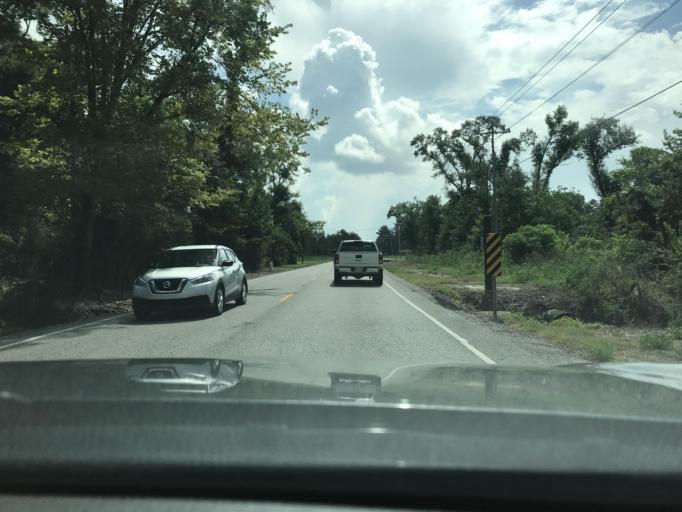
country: US
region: Louisiana
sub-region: Calcasieu Parish
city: Moss Bluff
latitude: 30.3447
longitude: -93.2118
